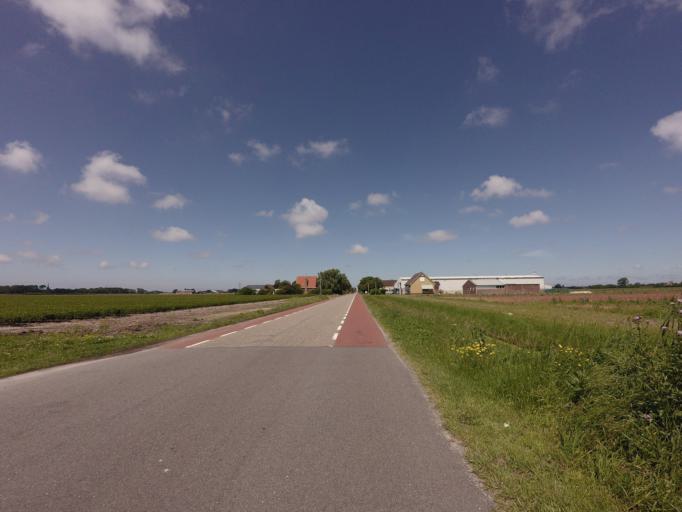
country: NL
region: North Holland
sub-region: Gemeente Den Helder
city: Den Helder
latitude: 52.8963
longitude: 4.8247
